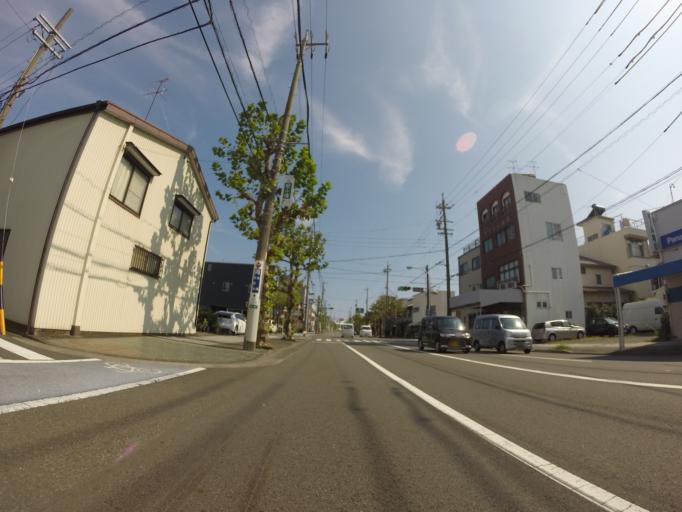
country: JP
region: Shizuoka
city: Shizuoka-shi
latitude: 34.9675
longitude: 138.3700
